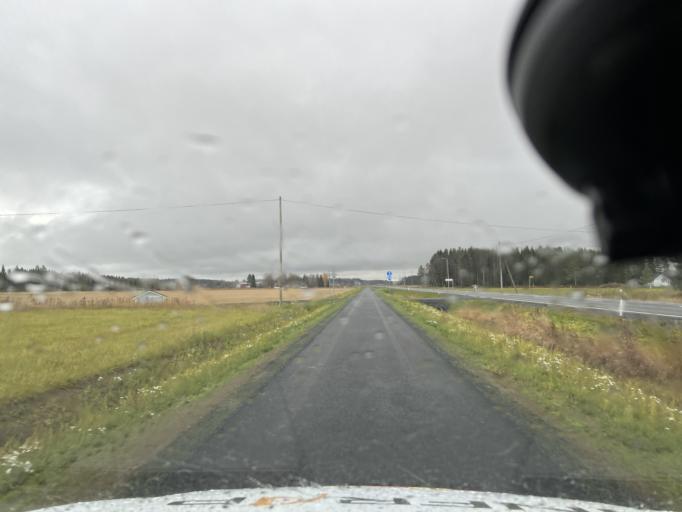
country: FI
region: Northern Ostrobothnia
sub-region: Ylivieska
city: Sievi
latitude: 63.9593
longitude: 24.5047
